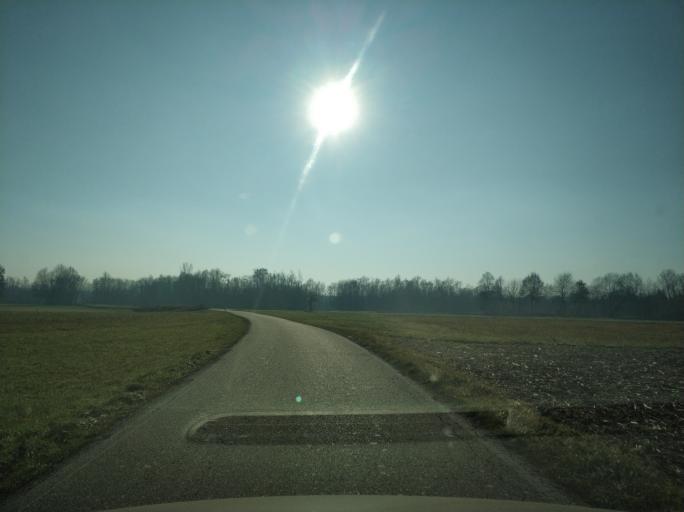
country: IT
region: Piedmont
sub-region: Provincia di Torino
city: Levone
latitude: 45.3106
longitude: 7.6120
